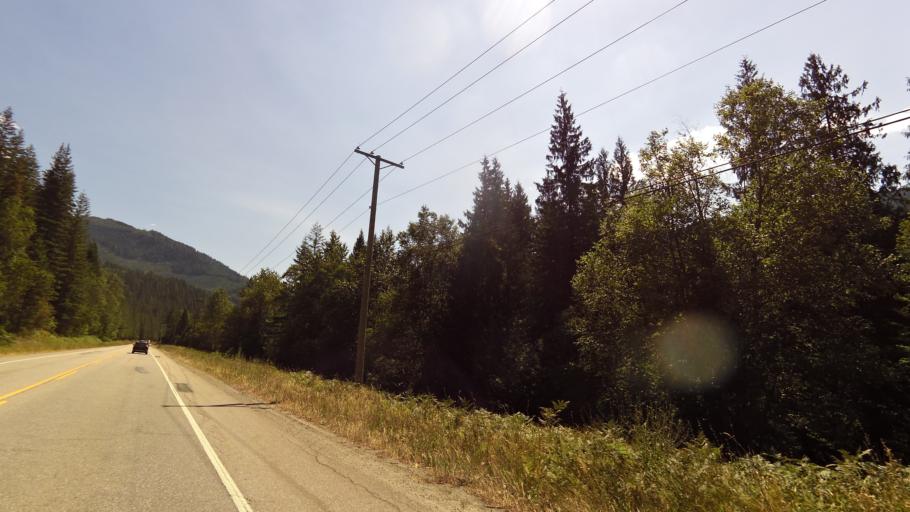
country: CA
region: British Columbia
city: Sicamous
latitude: 51.0030
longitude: -118.6633
